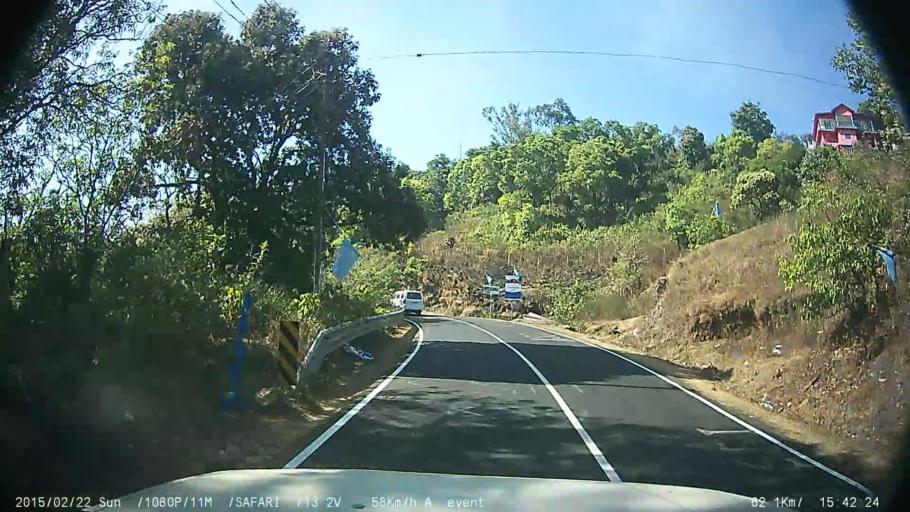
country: IN
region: Kerala
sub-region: Kottayam
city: Erattupetta
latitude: 9.5777
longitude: 76.9723
